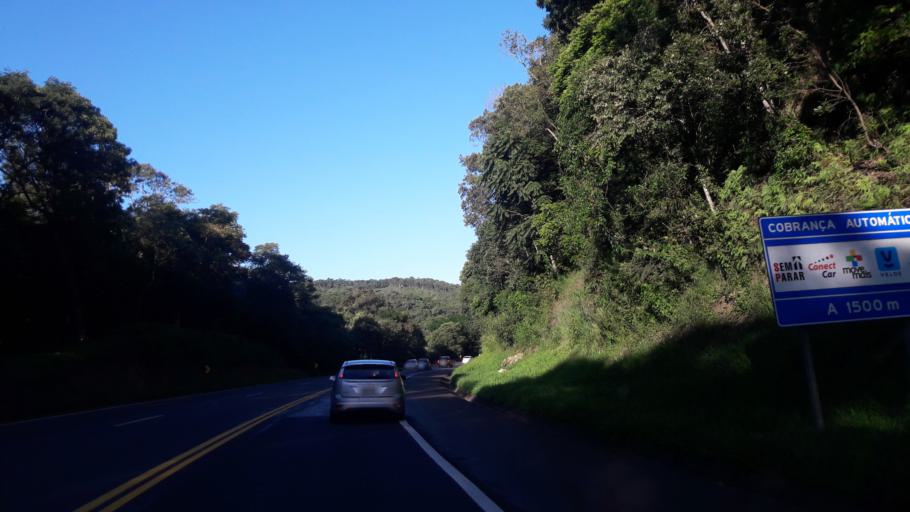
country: BR
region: Parana
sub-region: Prudentopolis
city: Prudentopolis
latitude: -25.3133
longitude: -51.1875
